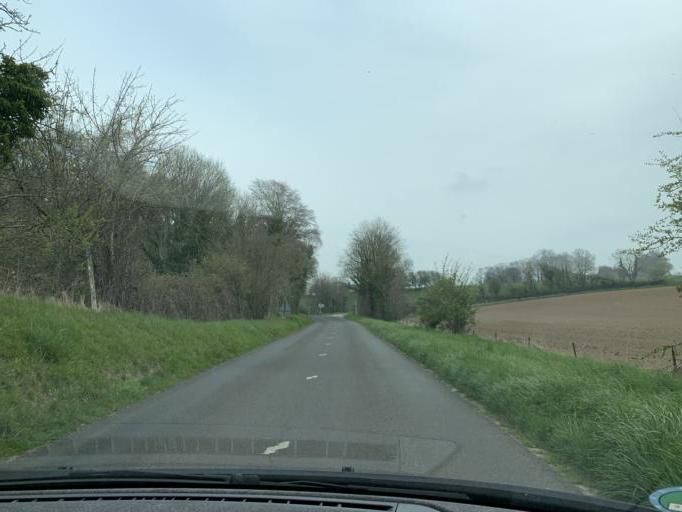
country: FR
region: Haute-Normandie
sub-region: Departement de la Seine-Maritime
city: Saint-Valery-en-Caux
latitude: 49.8525
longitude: 0.7335
